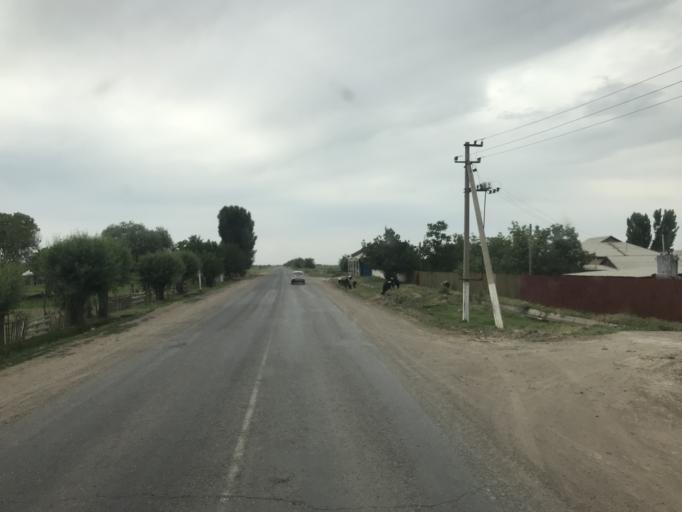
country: KZ
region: Ongtustik Qazaqstan
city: Asykata
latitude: 40.9067
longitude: 68.3532
